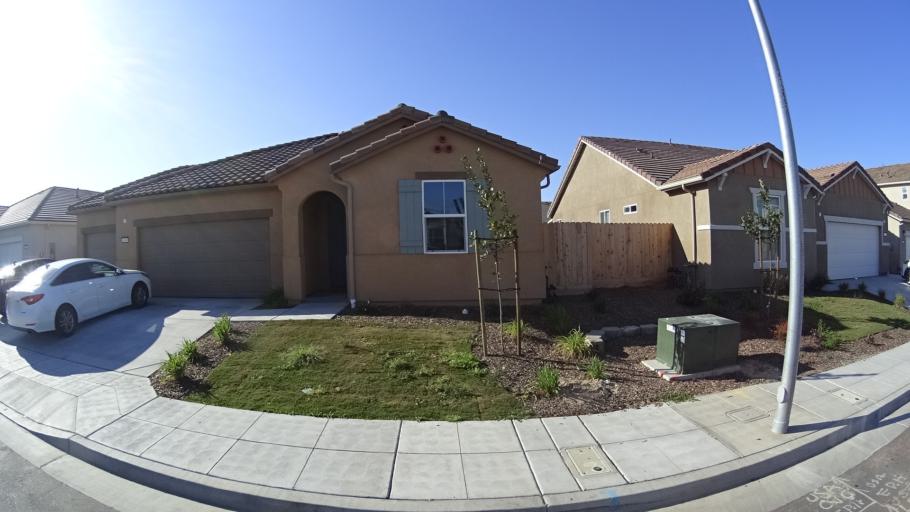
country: US
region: California
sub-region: Fresno County
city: West Park
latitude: 36.8026
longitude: -119.9047
